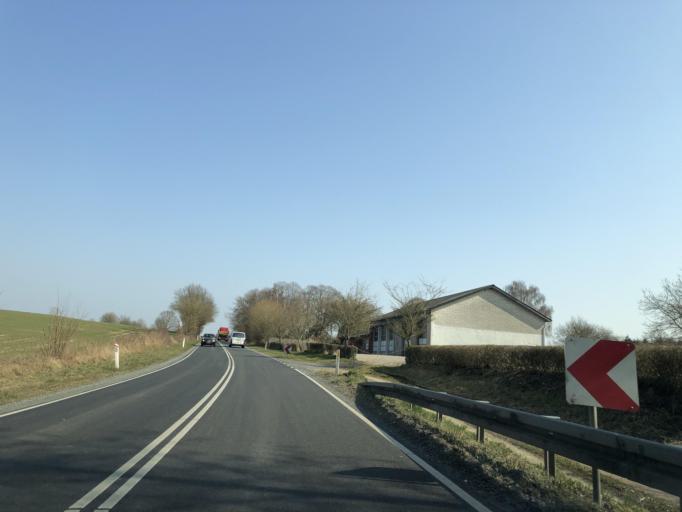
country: DK
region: South Denmark
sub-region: Sonderborg Kommune
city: Nordborg
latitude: 55.0254
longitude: 9.7754
